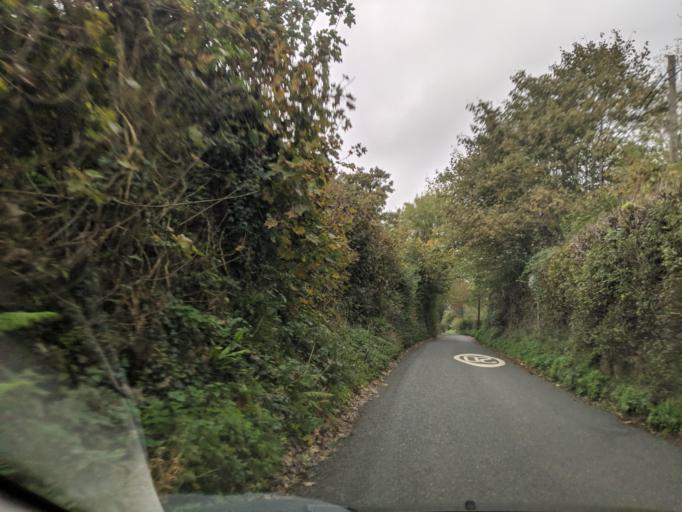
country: GB
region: England
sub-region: Cornwall
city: Saltash
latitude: 50.4421
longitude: -4.2193
